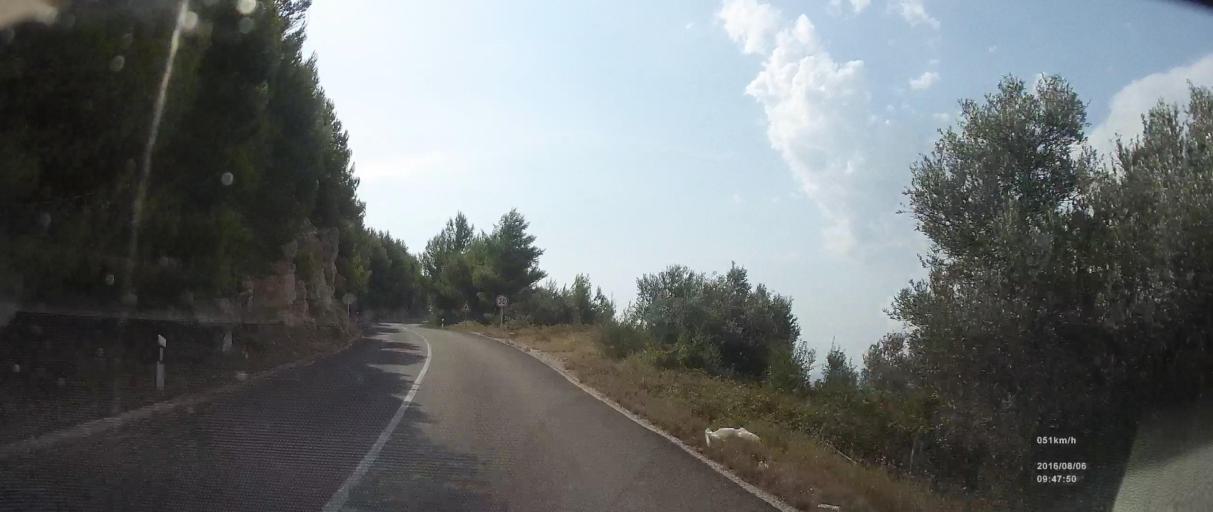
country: HR
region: Dubrovacko-Neretvanska
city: Blato
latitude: 42.7387
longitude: 17.5301
